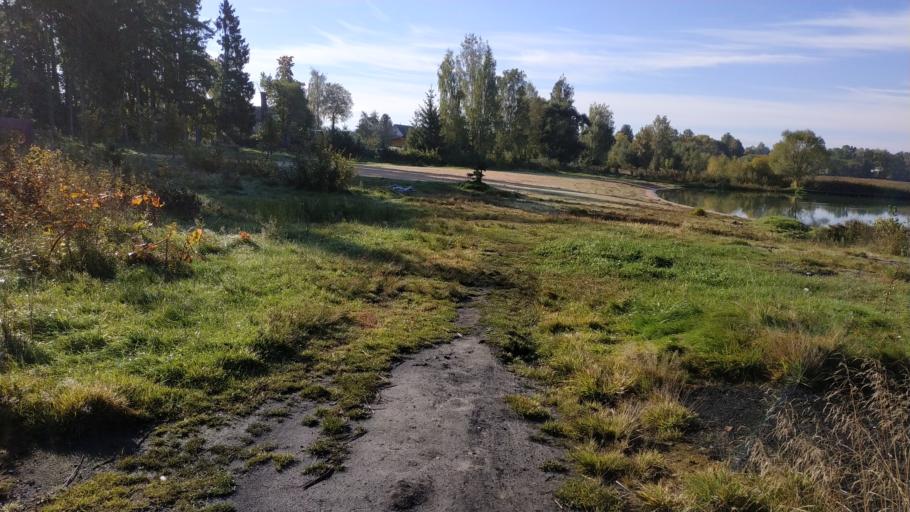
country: BY
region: Vitebsk
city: Vitebsk
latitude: 55.0902
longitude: 30.1651
